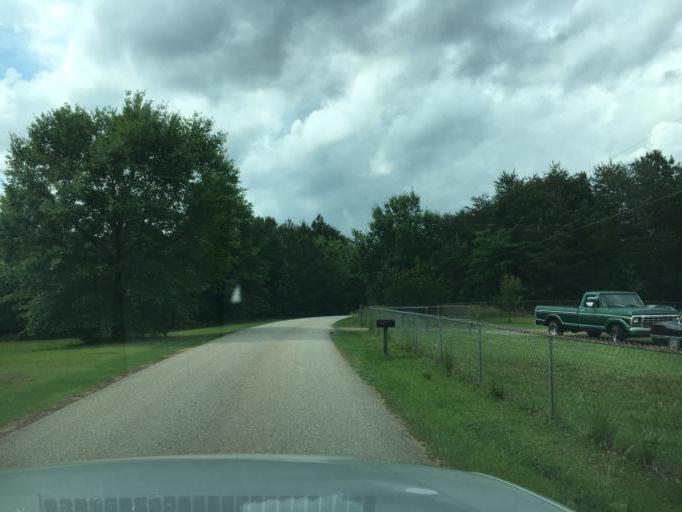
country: US
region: South Carolina
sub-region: Spartanburg County
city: Fairforest
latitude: 34.9140
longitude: -82.0386
